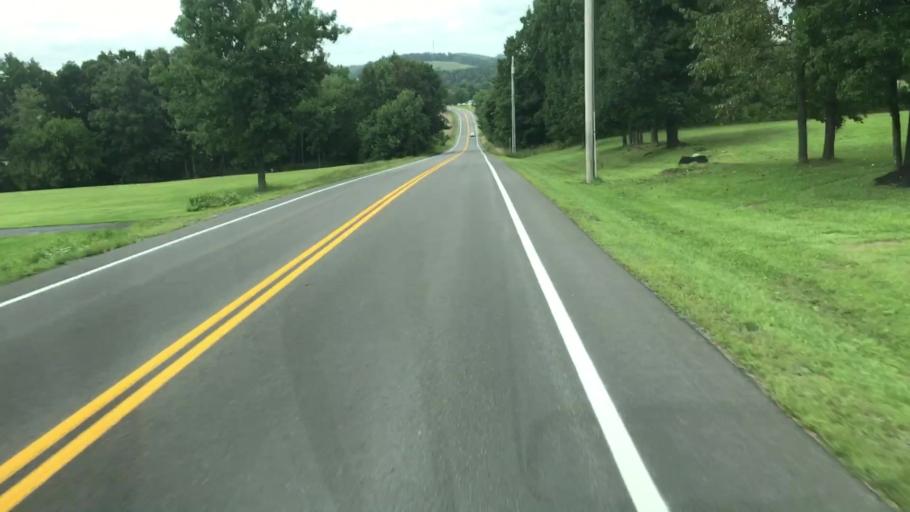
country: US
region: New York
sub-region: Onondaga County
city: Elbridge
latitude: 43.0022
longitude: -76.4398
